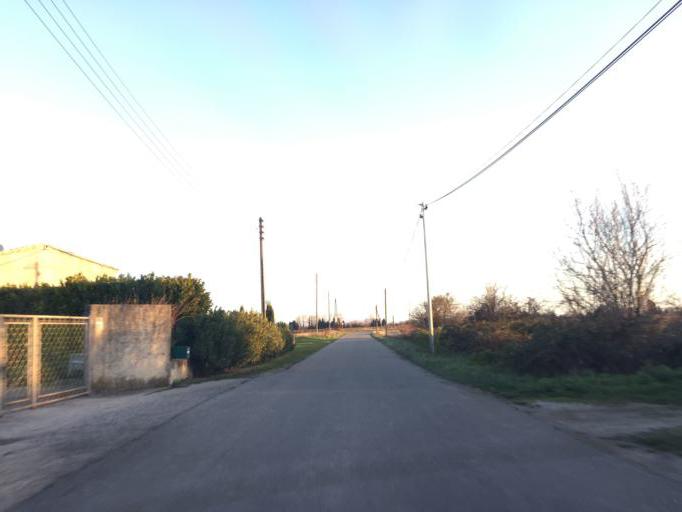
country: FR
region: Provence-Alpes-Cote d'Azur
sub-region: Departement du Vaucluse
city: Camaret-sur-Aigues
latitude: 44.1511
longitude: 4.8728
